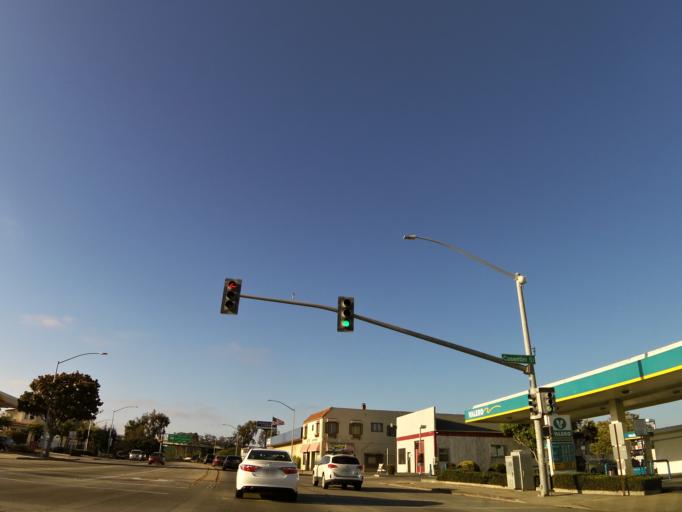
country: US
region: California
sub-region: Monterey County
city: Salinas
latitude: 36.6842
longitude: -121.6529
